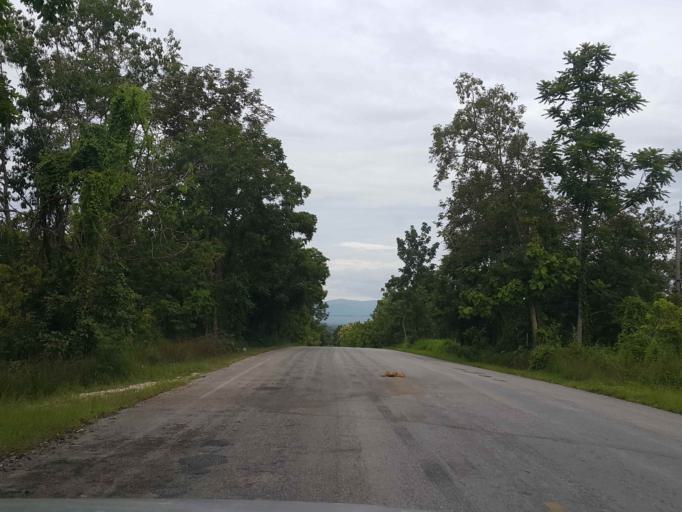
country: TH
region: Lampang
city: Thoen
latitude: 17.6301
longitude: 99.2463
